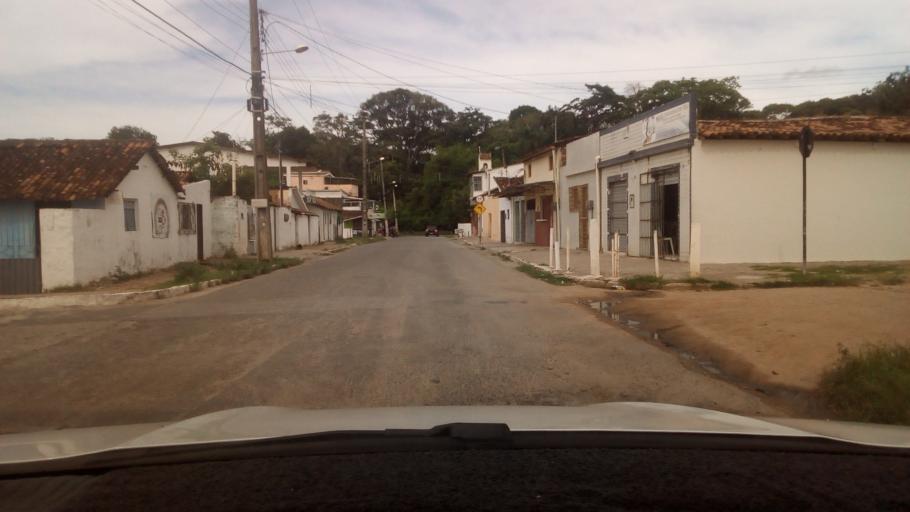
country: BR
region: Paraiba
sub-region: Joao Pessoa
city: Joao Pessoa
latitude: -7.1457
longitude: -34.8708
